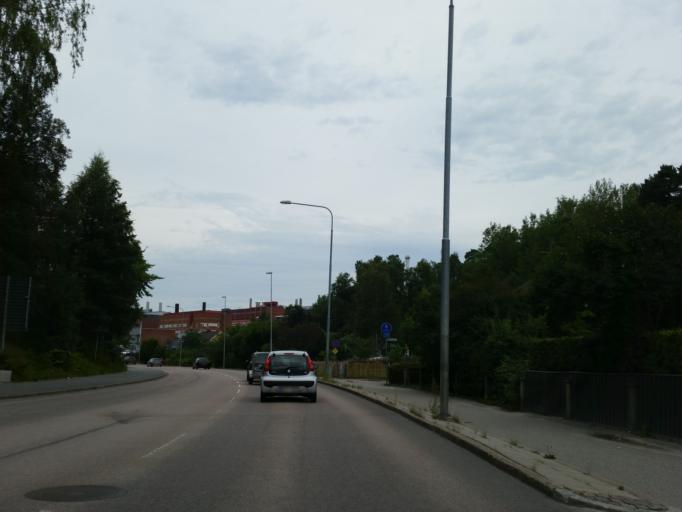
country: SE
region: Stockholm
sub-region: Sodertalje Kommun
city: Soedertaelje
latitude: 59.2009
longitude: 17.6172
